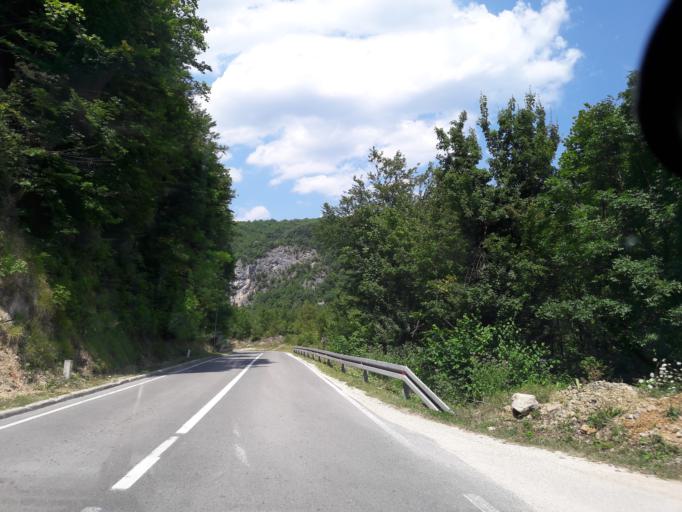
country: BA
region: Republika Srpska
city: Sipovo
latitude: 44.2199
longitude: 17.1193
